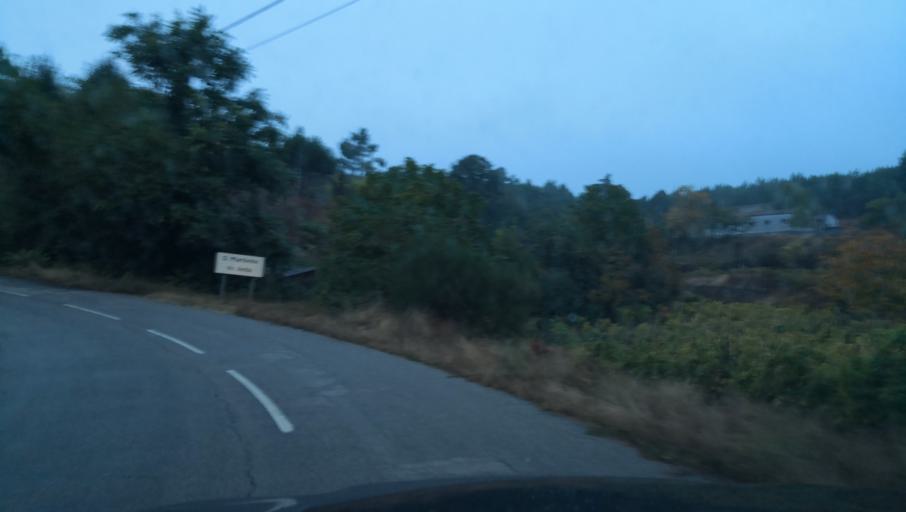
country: PT
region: Vila Real
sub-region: Sabrosa
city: Sabrosa
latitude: 41.2659
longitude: -7.6067
